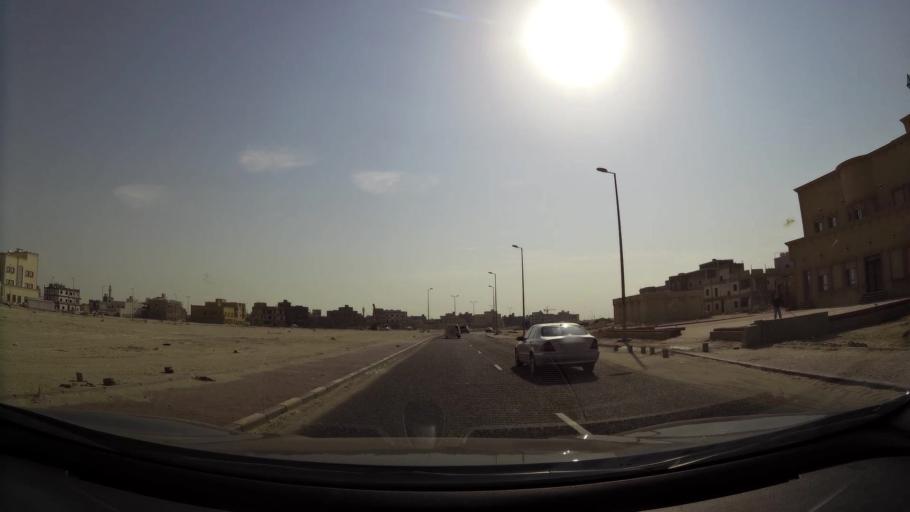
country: KW
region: Al Ahmadi
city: Al Wafrah
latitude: 28.7870
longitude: 48.0466
